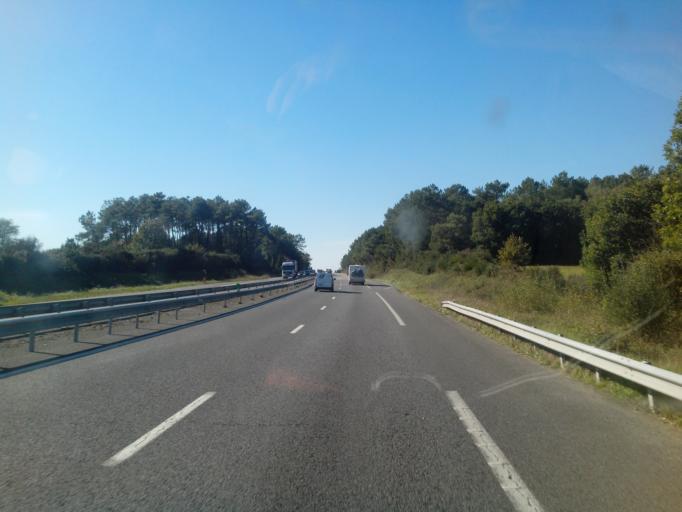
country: FR
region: Brittany
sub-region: Departement du Morbihan
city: Marzan
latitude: 47.5362
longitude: -2.3413
